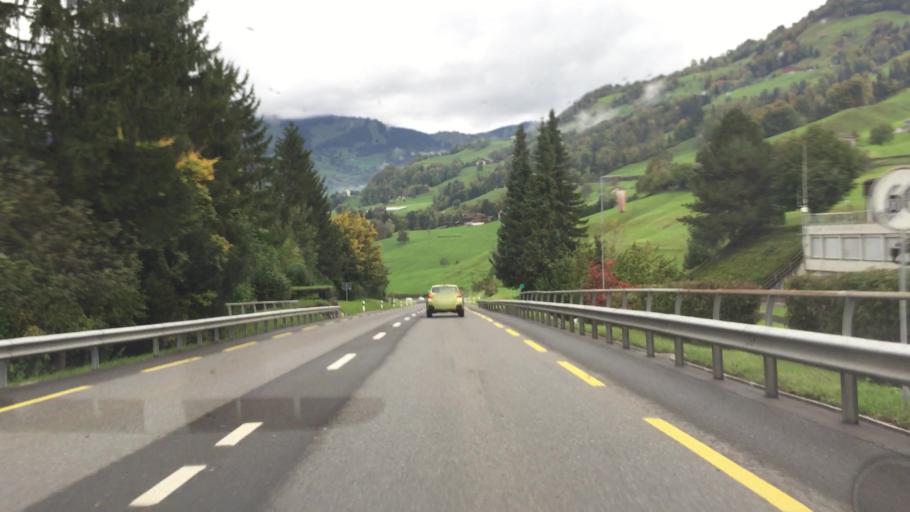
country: CH
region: Schwyz
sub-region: Bezirk Schwyz
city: Schwyz
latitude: 47.0312
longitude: 8.6424
